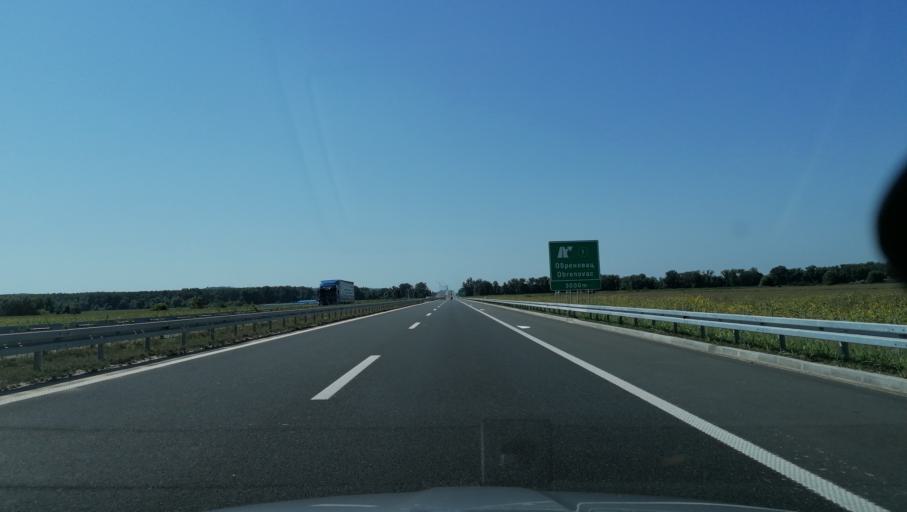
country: RS
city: Baric
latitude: 44.6779
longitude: 20.2584
